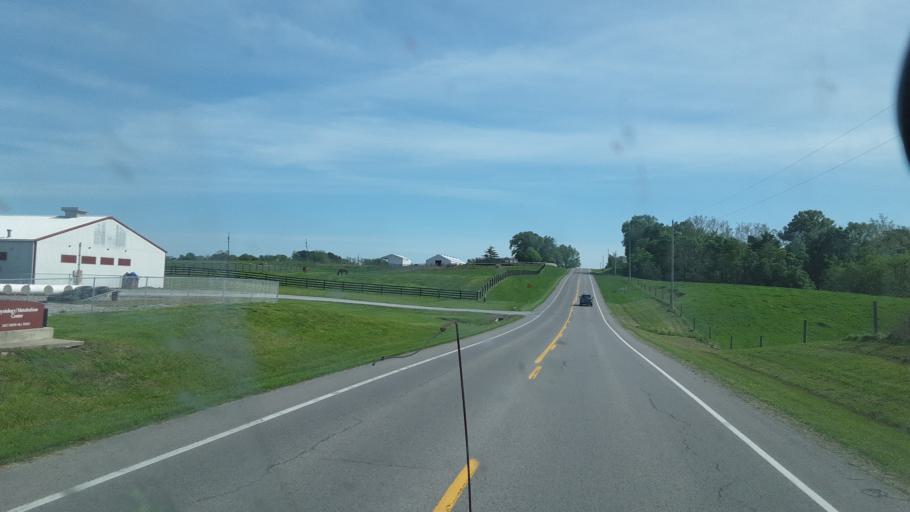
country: US
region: Illinois
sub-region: Jackson County
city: Carbondale
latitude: 37.6963
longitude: -89.2473
